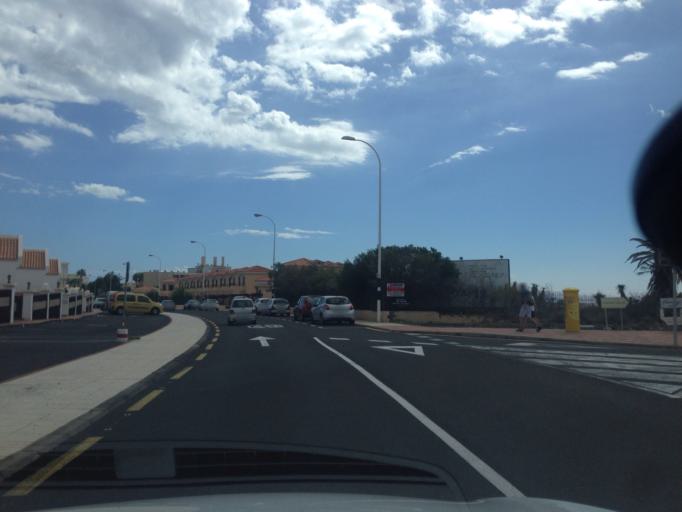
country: ES
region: Canary Islands
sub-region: Provincia de Santa Cruz de Tenerife
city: Las Rosas
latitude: 28.0319
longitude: -16.6118
